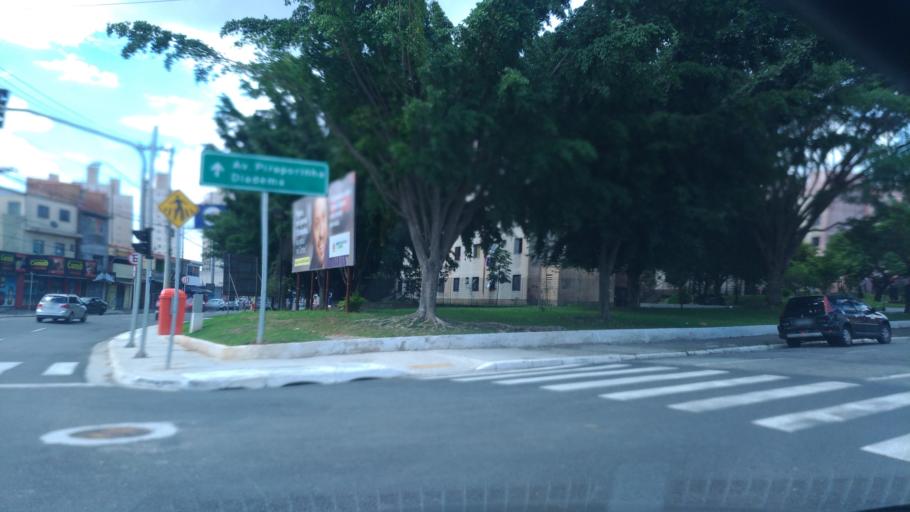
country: BR
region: Sao Paulo
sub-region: Sao Bernardo Do Campo
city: Sao Bernardo do Campo
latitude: -23.7078
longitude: -46.5886
